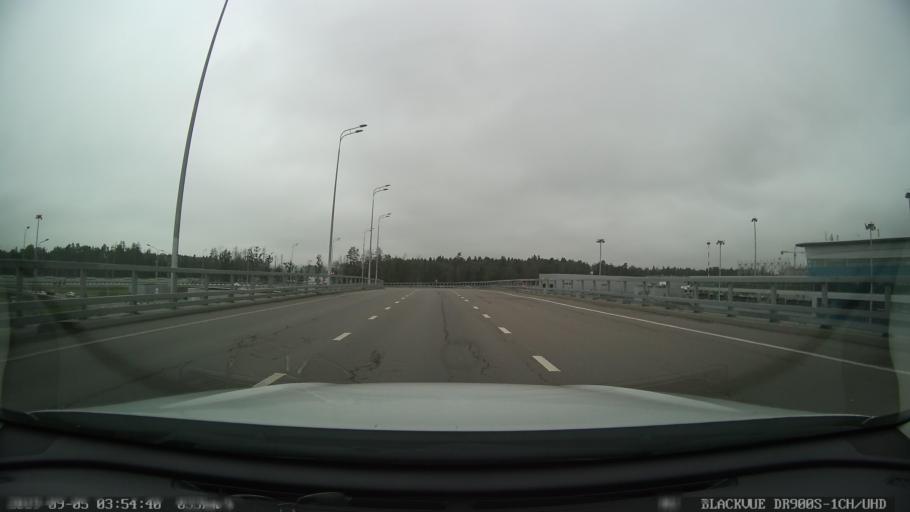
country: RU
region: Moskovskaya
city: Novopodrezkovo
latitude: 55.9627
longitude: 37.4042
